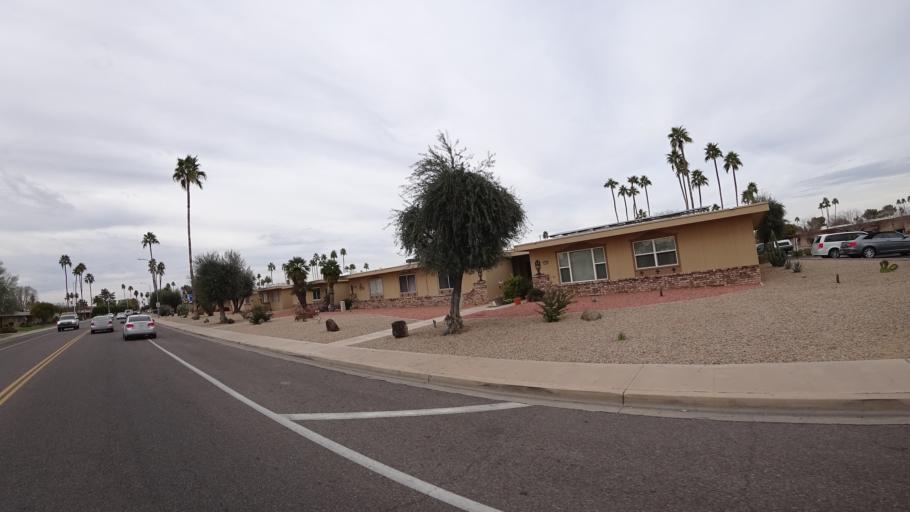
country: US
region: Arizona
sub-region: Maricopa County
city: Youngtown
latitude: 33.6073
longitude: -112.2949
